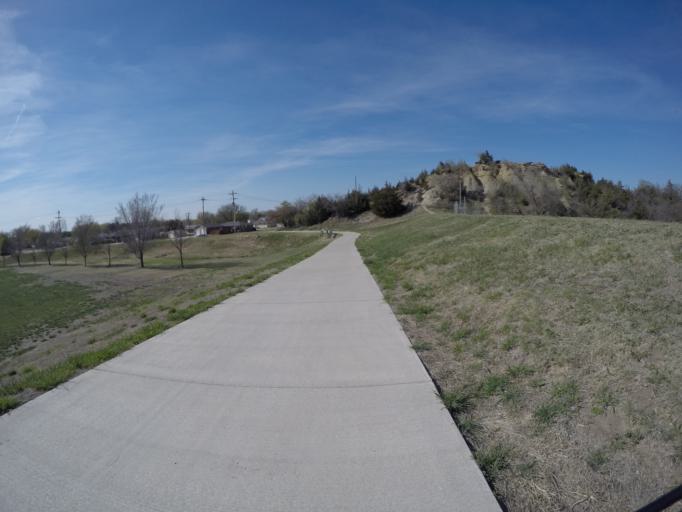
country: US
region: Kansas
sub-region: Saline County
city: Salina
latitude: 38.8324
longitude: -97.5890
